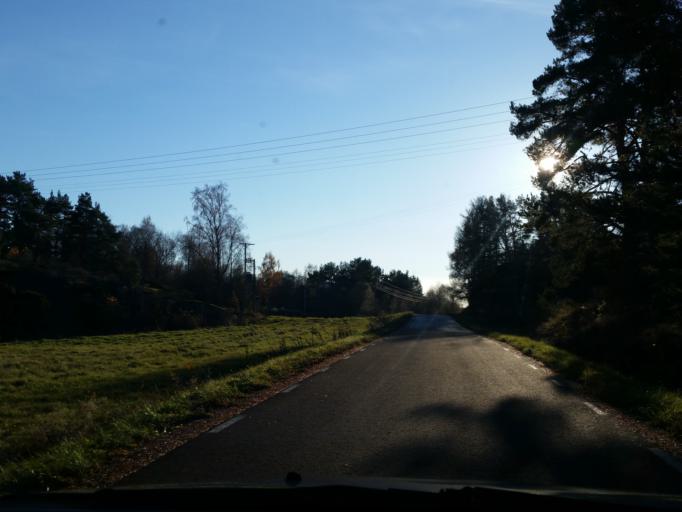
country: AX
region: Alands skaergard
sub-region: Braendoe
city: Braendoe
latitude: 60.4159
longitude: 21.0535
